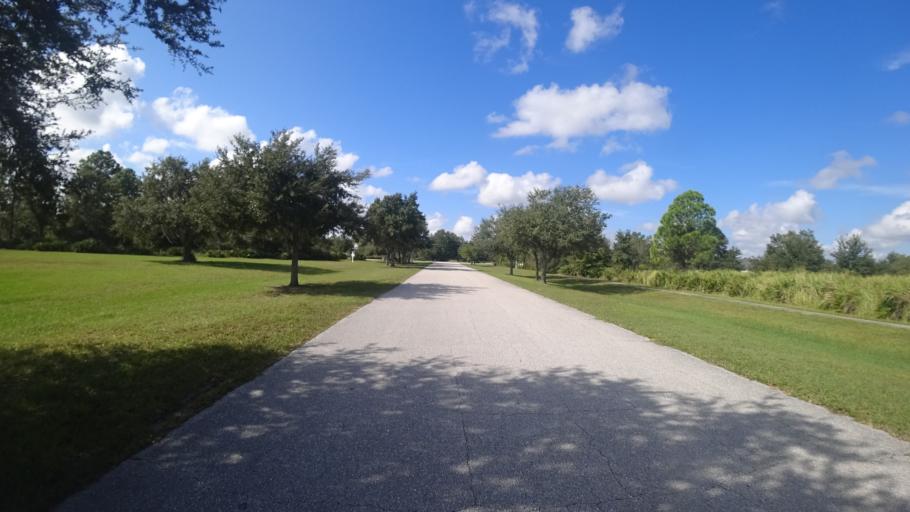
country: US
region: Florida
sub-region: Sarasota County
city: The Meadows
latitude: 27.3988
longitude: -82.3212
